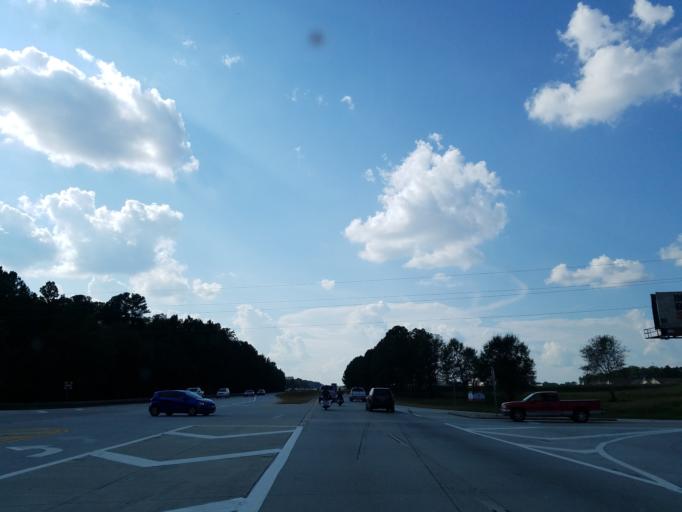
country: US
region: Georgia
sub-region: Barrow County
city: Russell
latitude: 33.9398
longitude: -83.7363
